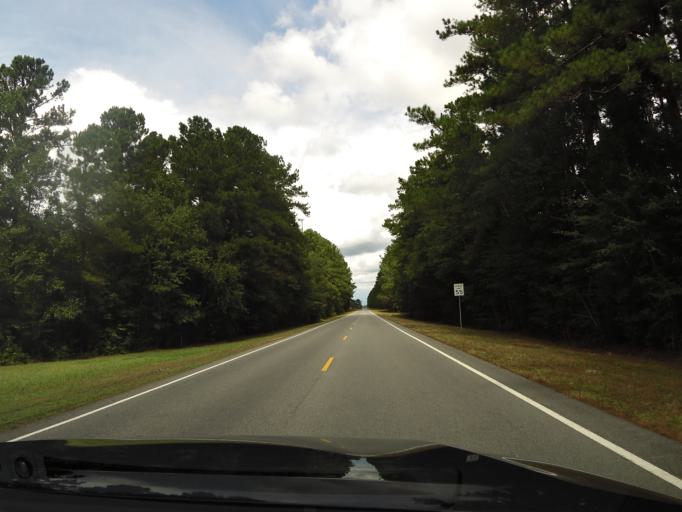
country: US
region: Georgia
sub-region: Brantley County
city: Nahunta
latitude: 31.0669
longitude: -82.0133
